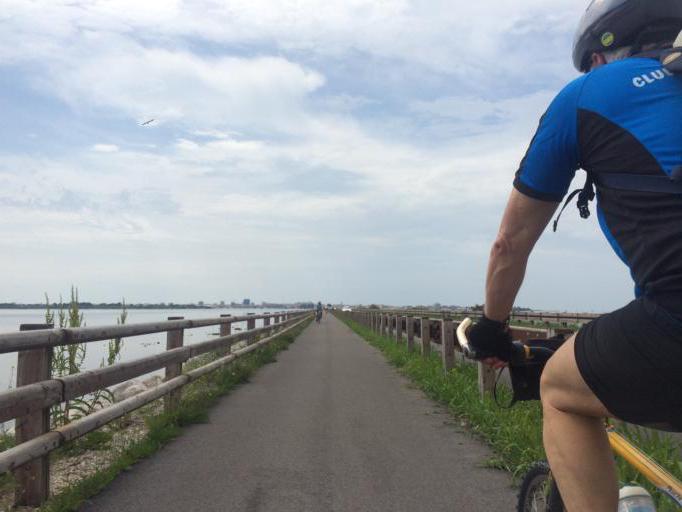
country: IT
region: Friuli Venezia Giulia
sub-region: Provincia di Gorizia
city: Grado
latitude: 45.7047
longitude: 13.3827
